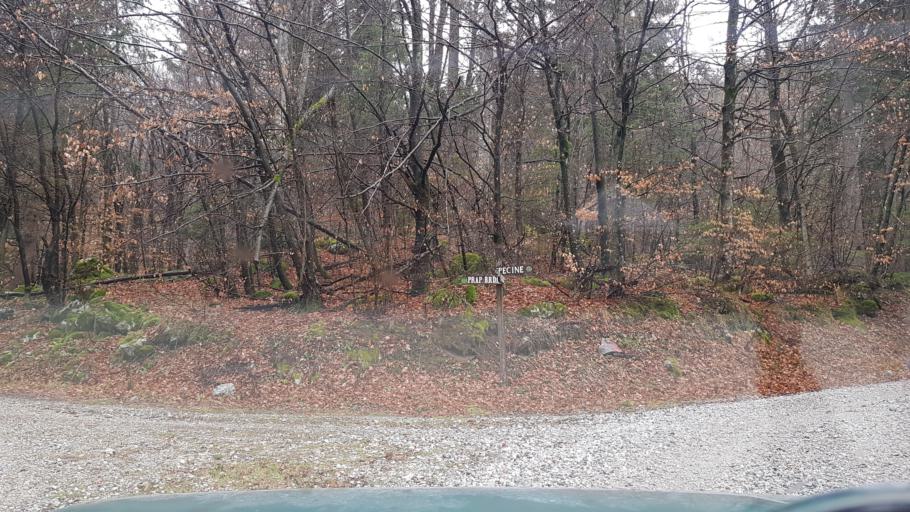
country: SI
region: Cerkno
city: Cerkno
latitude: 46.1343
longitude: 13.8617
